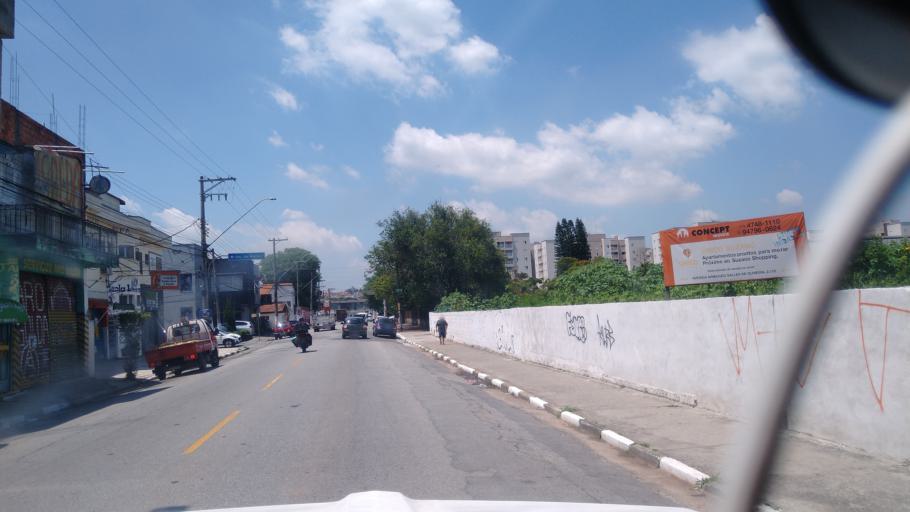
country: BR
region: Sao Paulo
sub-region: Suzano
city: Suzano
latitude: -23.5449
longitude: -46.3168
